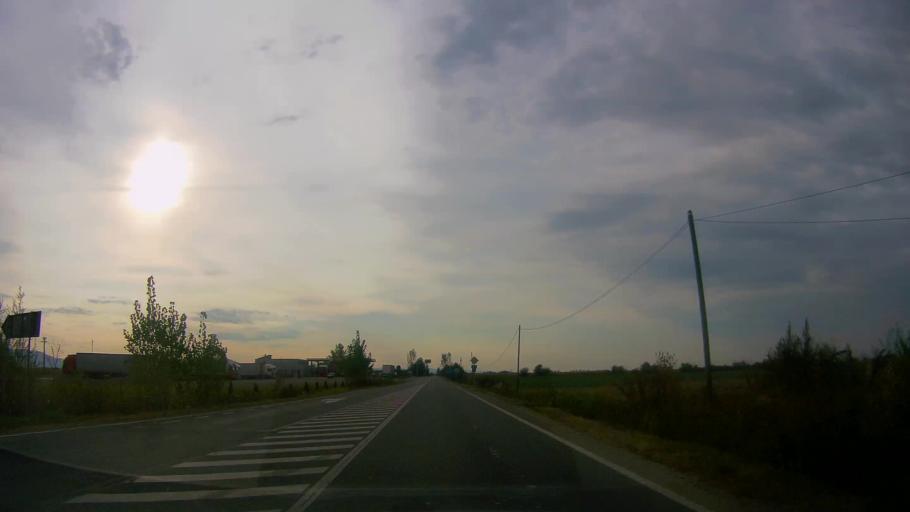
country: RO
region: Satu Mare
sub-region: Comuna Turulung
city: Turulung
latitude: 47.9577
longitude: 23.0552
